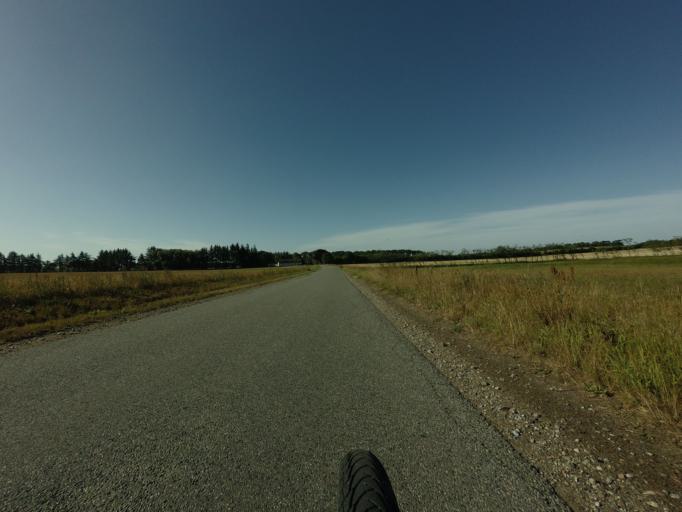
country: DK
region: North Denmark
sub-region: Hjorring Kommune
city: Vra
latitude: 57.3741
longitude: 10.0037
